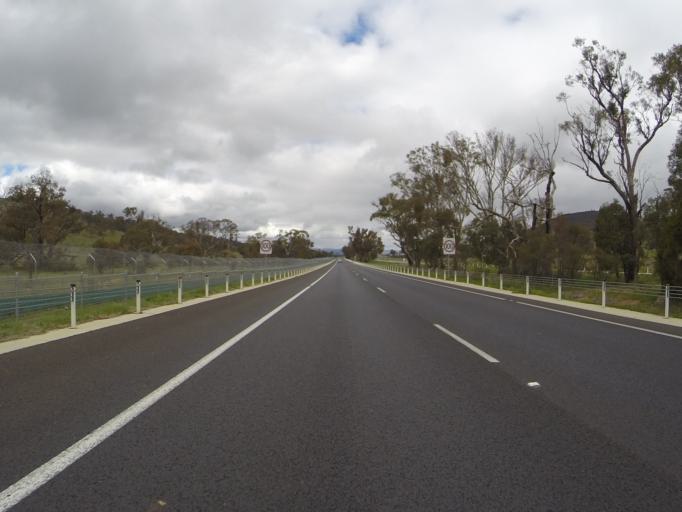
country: AU
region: Australian Capital Territory
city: Kaleen
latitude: -35.2200
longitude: 149.1960
